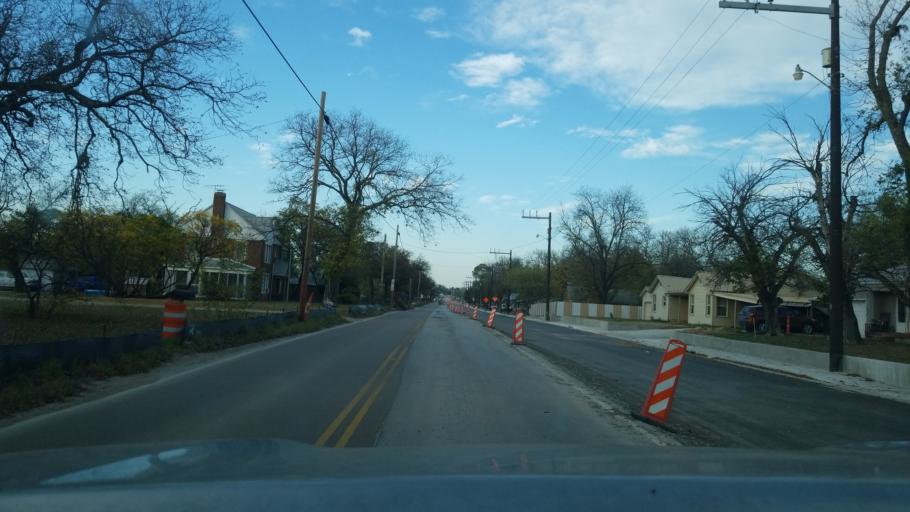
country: US
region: Texas
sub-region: Brown County
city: Lake Brownwood
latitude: 32.0901
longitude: -98.9640
